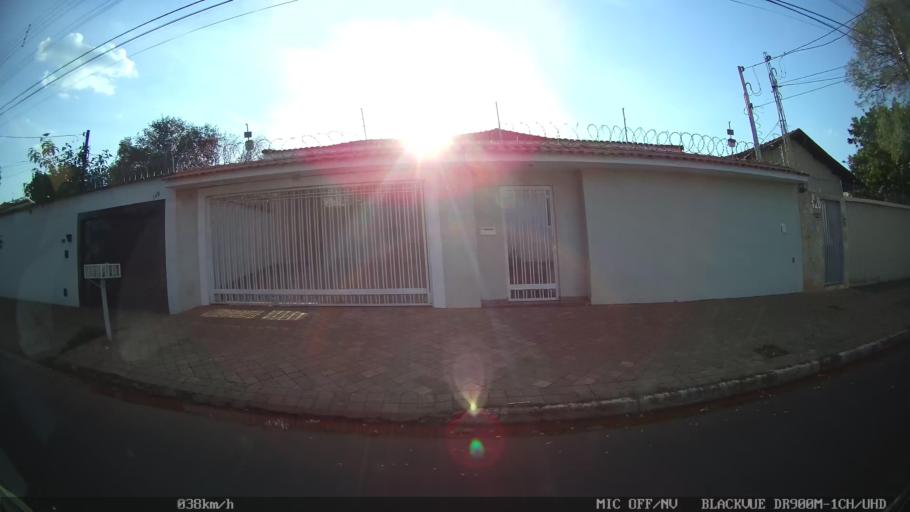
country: BR
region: Sao Paulo
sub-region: Ribeirao Preto
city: Ribeirao Preto
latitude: -21.1582
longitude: -47.8396
